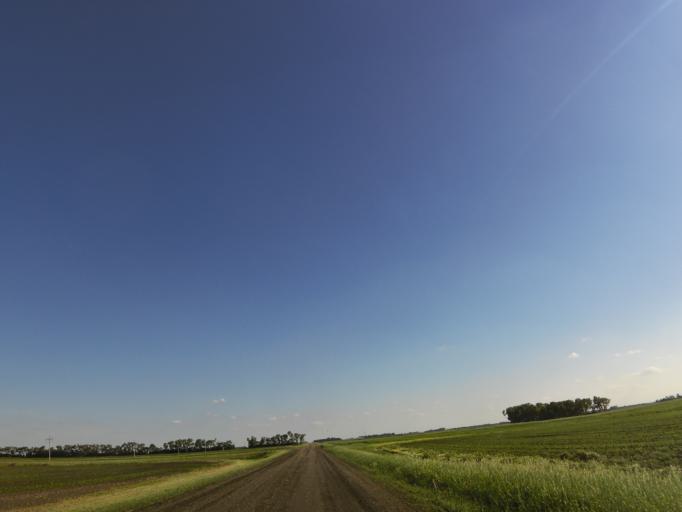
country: US
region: North Dakota
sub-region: Walsh County
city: Grafton
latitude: 48.3987
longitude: -97.2338
